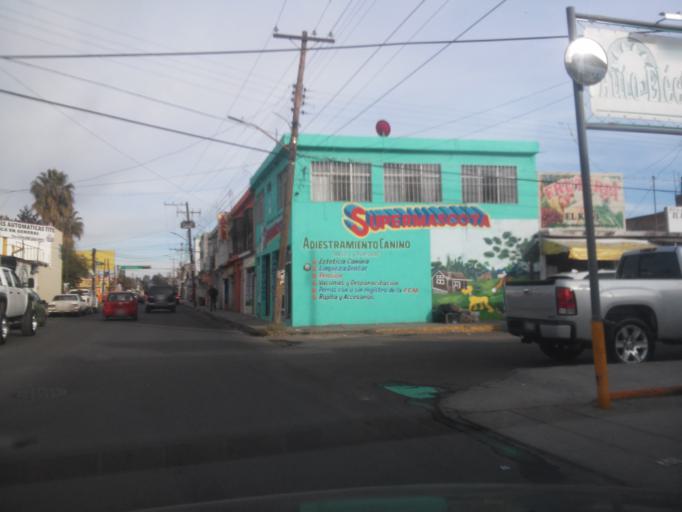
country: MX
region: Durango
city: Victoria de Durango
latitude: 24.0258
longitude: -104.6468
